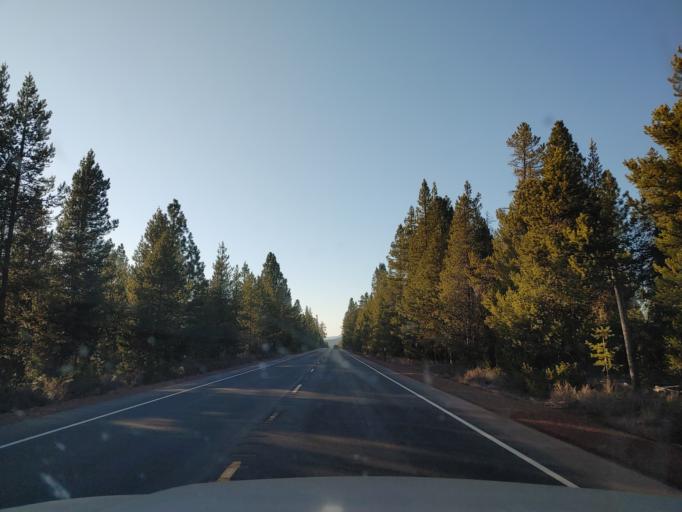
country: US
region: Oregon
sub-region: Deschutes County
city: La Pine
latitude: 43.3893
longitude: -121.8099
